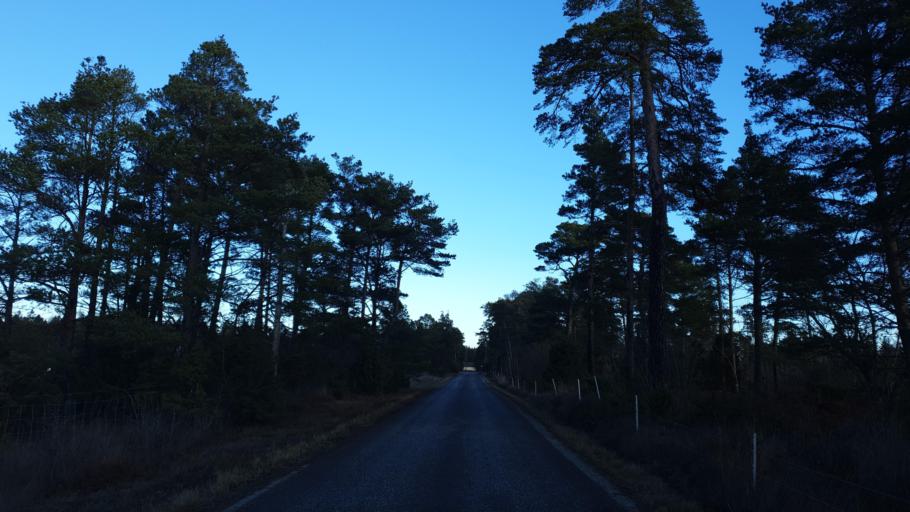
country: SE
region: Gotland
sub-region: Gotland
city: Slite
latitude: 57.3801
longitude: 18.8054
